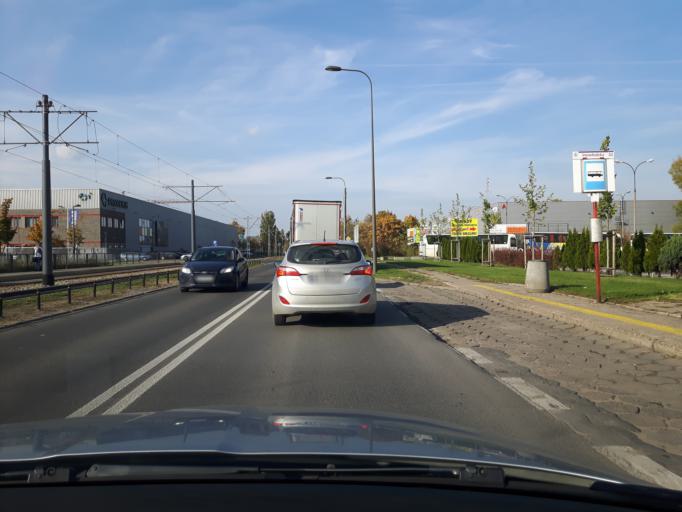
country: PL
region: Masovian Voivodeship
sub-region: Warszawa
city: Targowek
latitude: 52.3015
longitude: 21.0213
